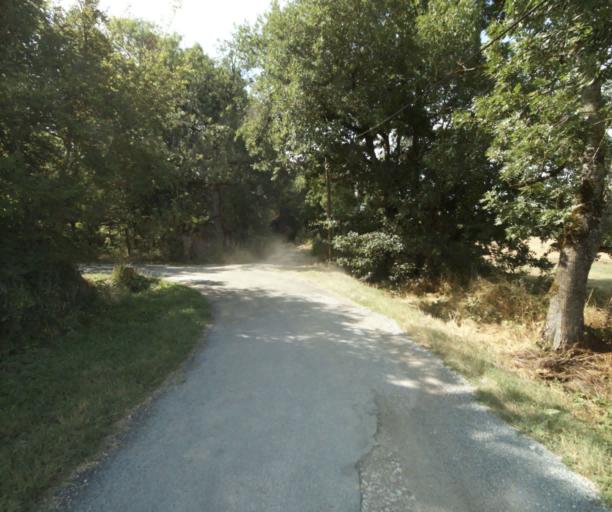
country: FR
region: Midi-Pyrenees
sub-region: Departement du Tarn
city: Soual
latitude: 43.5228
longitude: 2.0950
